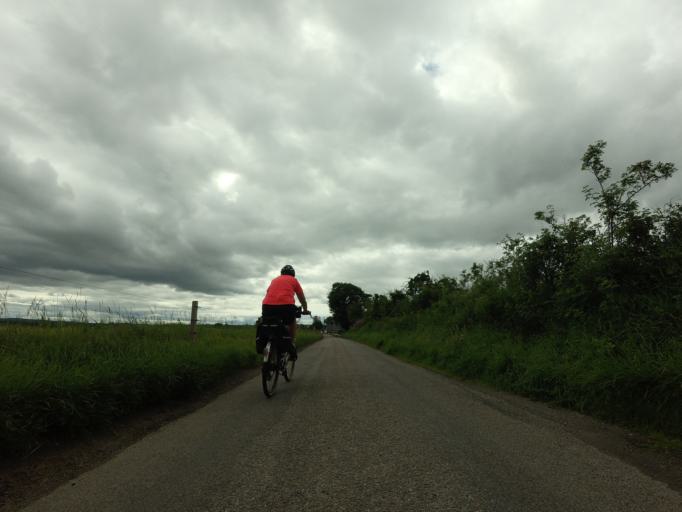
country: GB
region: Scotland
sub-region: Moray
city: Forres
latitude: 57.6080
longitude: -3.6909
